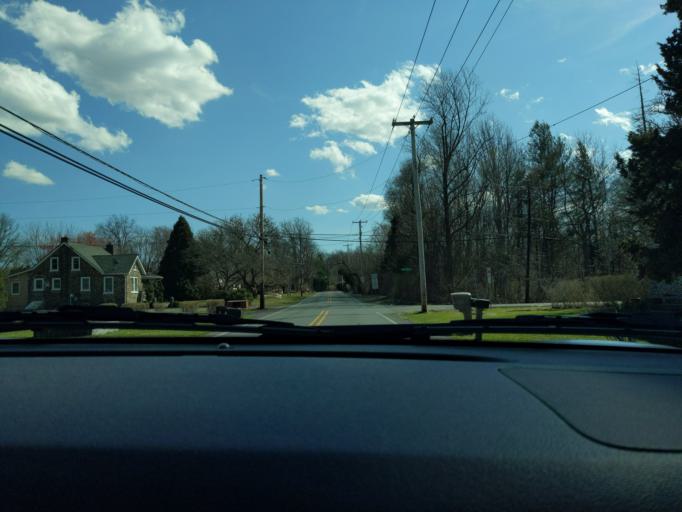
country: US
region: Pennsylvania
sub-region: Bucks County
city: Richlandtown
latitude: 40.4672
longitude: -75.2736
